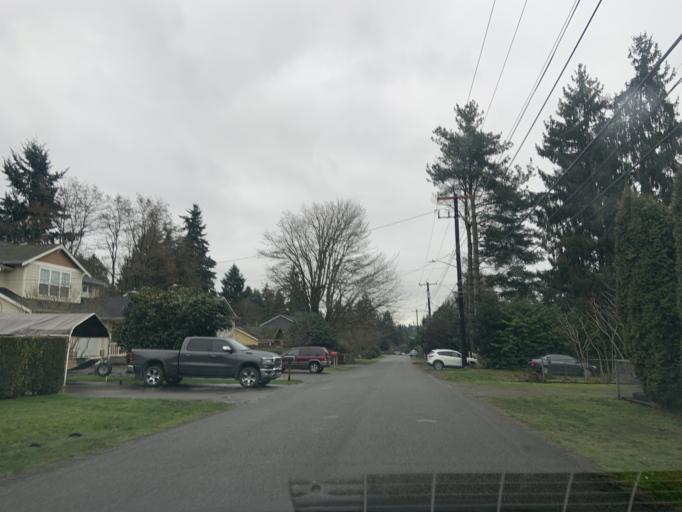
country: US
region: Washington
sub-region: King County
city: Lake Forest Park
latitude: 47.7155
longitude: -122.2853
